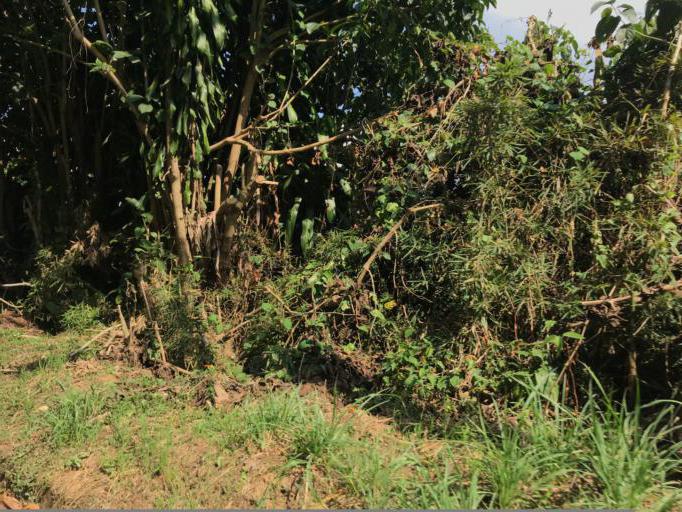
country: CO
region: Valle del Cauca
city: Cali
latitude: 3.4695
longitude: -76.6238
